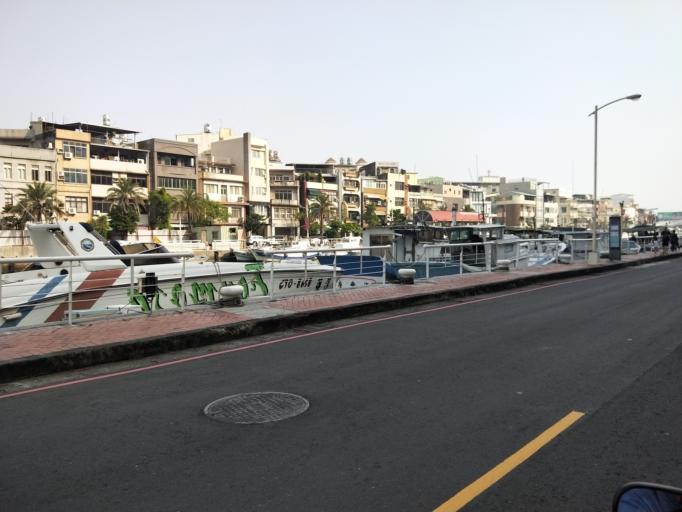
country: TW
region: Kaohsiung
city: Kaohsiung
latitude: 22.6230
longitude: 120.2693
